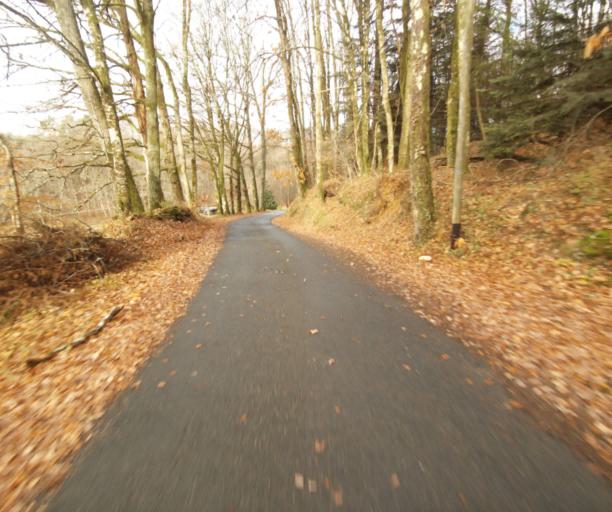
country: FR
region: Limousin
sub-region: Departement de la Correze
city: Saint-Mexant
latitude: 45.2543
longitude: 1.6437
